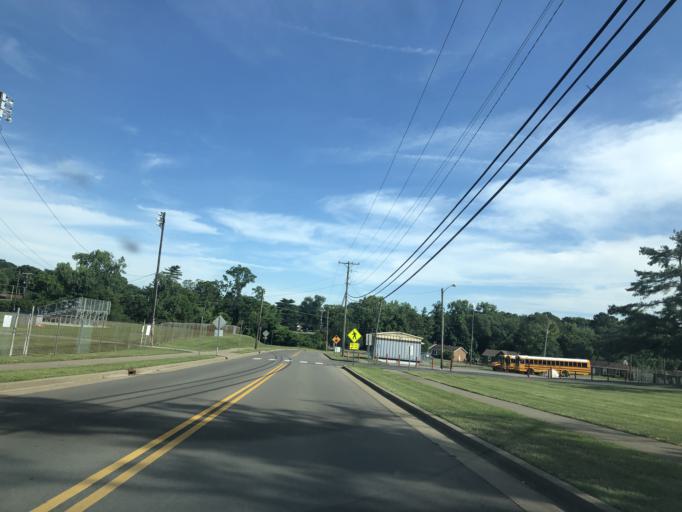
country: US
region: Tennessee
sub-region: Davidson County
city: Belle Meade
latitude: 36.0708
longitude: -86.9340
